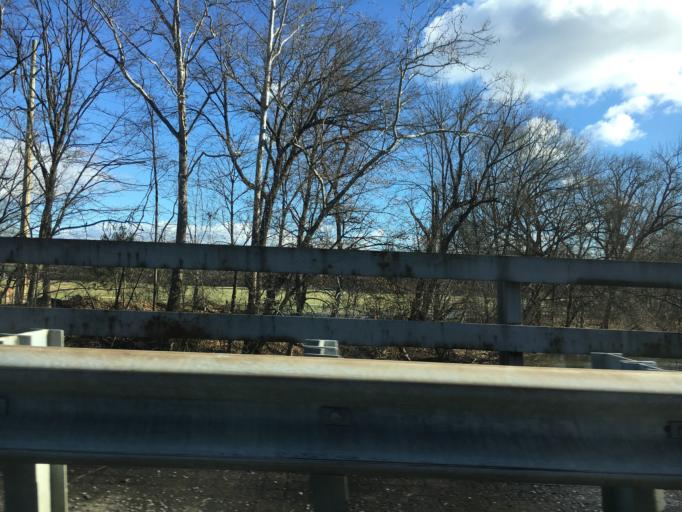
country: US
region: Pennsylvania
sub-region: Lehigh County
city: Allentown
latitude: 40.6271
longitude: -75.5096
